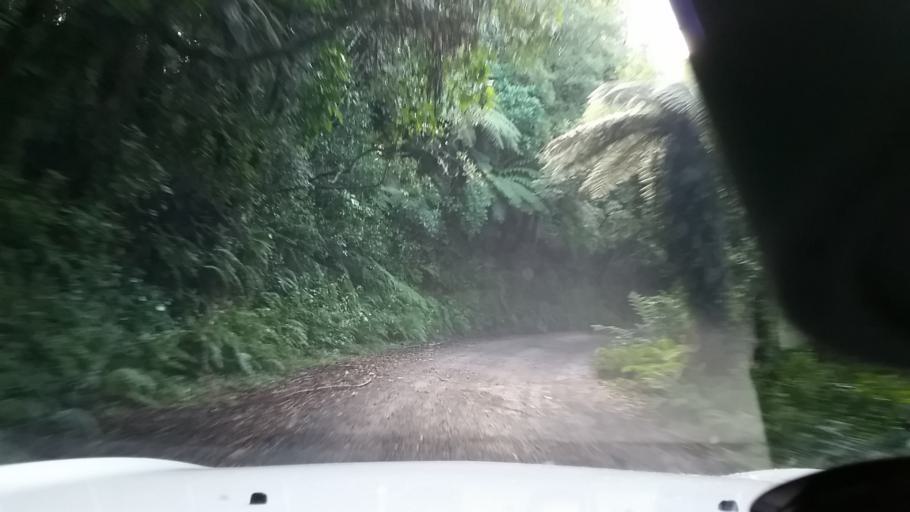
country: NZ
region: Bay of Plenty
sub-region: Kawerau District
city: Kawerau
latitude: -38.0191
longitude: 176.5944
